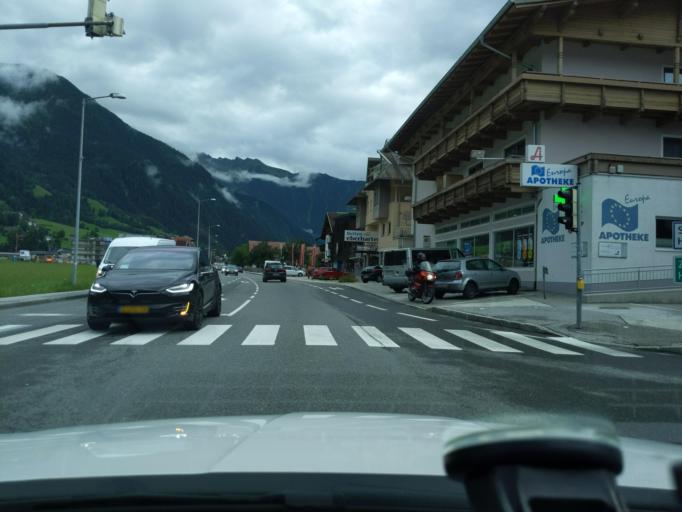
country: AT
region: Tyrol
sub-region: Politischer Bezirk Schwaz
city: Ramsau im Zillertal
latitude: 47.2044
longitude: 11.8706
